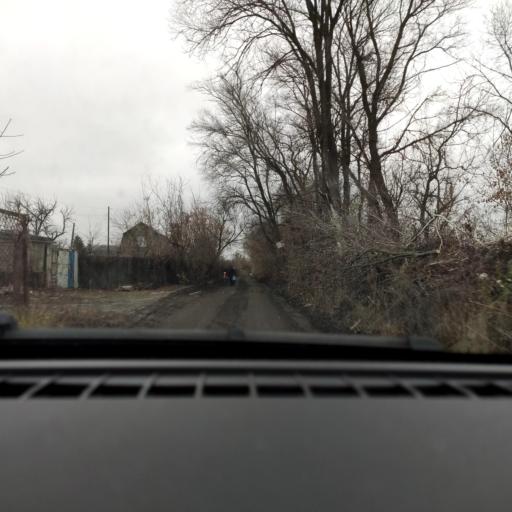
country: RU
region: Voronezj
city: Maslovka
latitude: 51.6078
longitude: 39.2719
